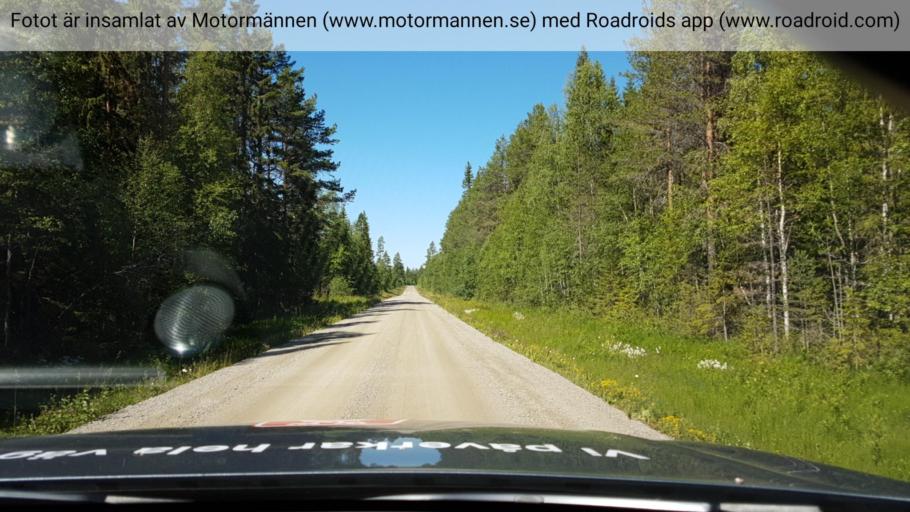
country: SE
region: Jaemtland
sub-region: Braecke Kommun
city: Braecke
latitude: 62.8004
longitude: 15.2430
